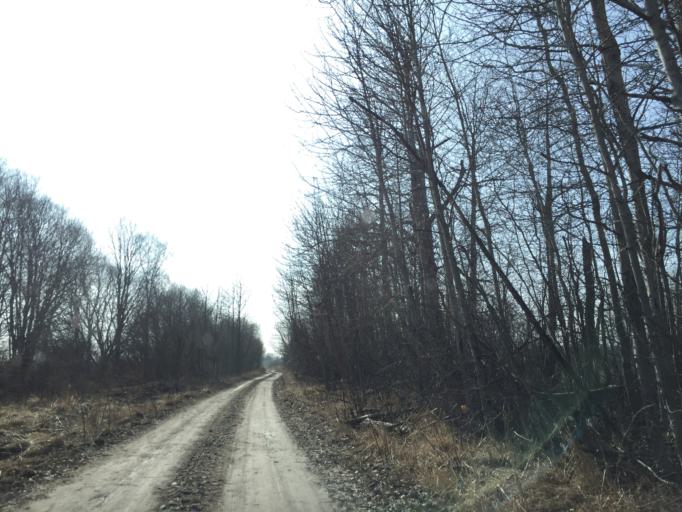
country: LV
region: Dundaga
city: Dundaga
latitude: 57.9320
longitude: 22.0640
